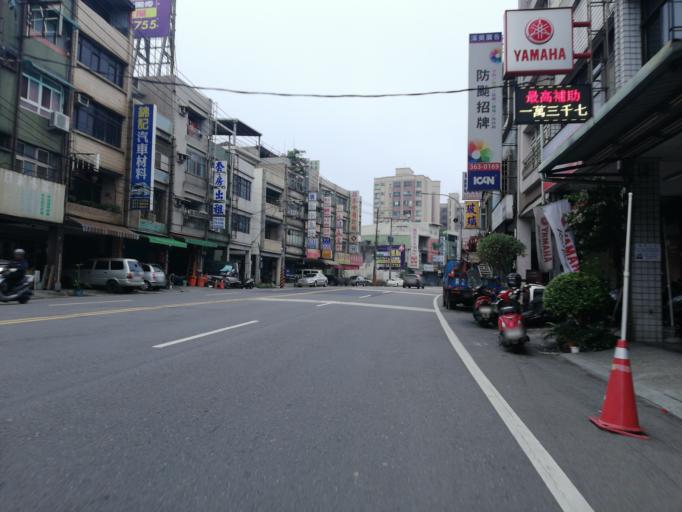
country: TW
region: Taiwan
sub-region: Taoyuan
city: Taoyuan
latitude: 24.9847
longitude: 121.3104
